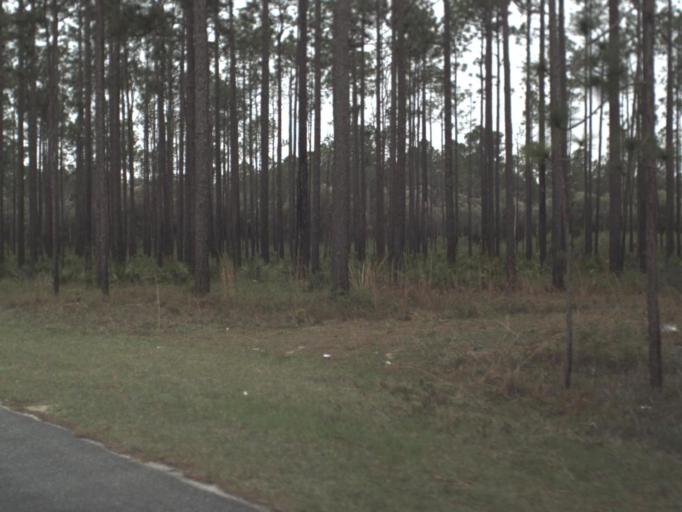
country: US
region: Florida
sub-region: Franklin County
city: Apalachicola
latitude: 29.9795
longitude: -84.9754
